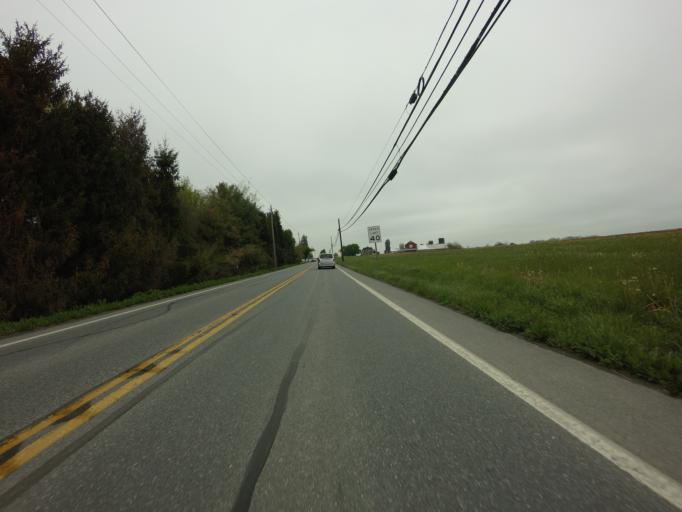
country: US
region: Maryland
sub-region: Carroll County
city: New Windsor
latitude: 39.5161
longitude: -77.1094
